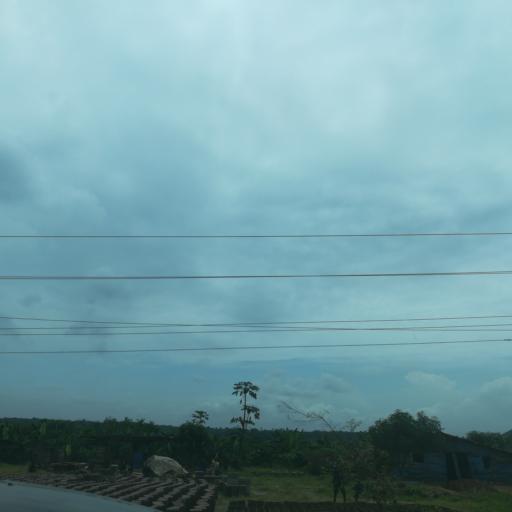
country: NG
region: Lagos
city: Ejirin
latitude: 6.6503
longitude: 3.7129
